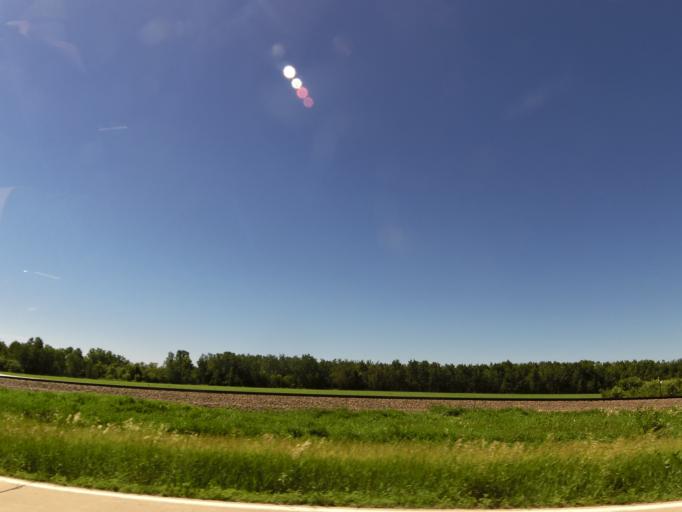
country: US
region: Minnesota
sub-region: Red Lake County
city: Red Lake Falls
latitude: 47.6960
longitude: -96.1279
